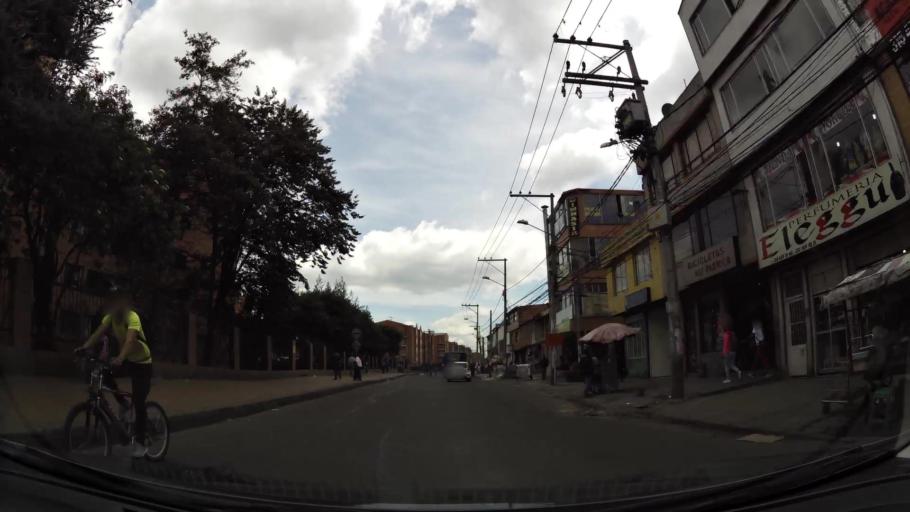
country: CO
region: Cundinamarca
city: Cota
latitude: 4.7319
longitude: -74.0866
